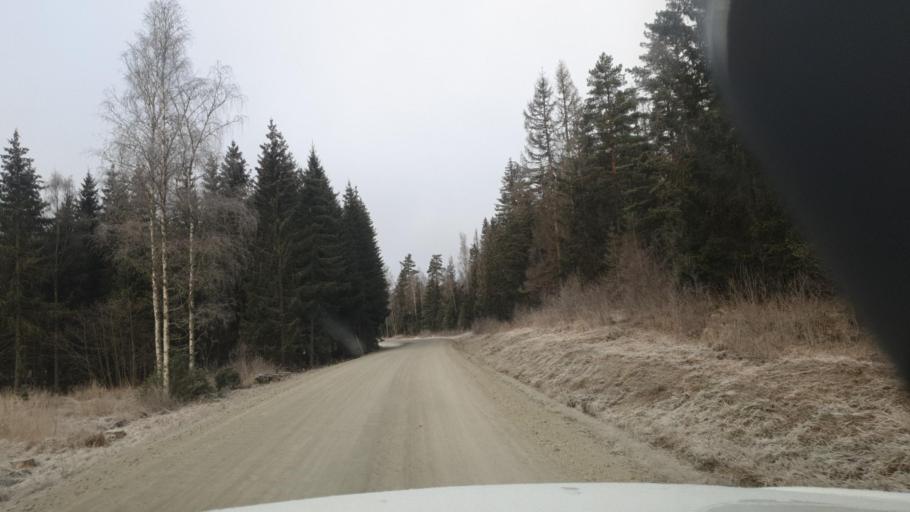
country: SE
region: Vaermland
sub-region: Karlstads Kommun
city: Edsvalla
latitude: 59.4486
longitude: 13.1546
